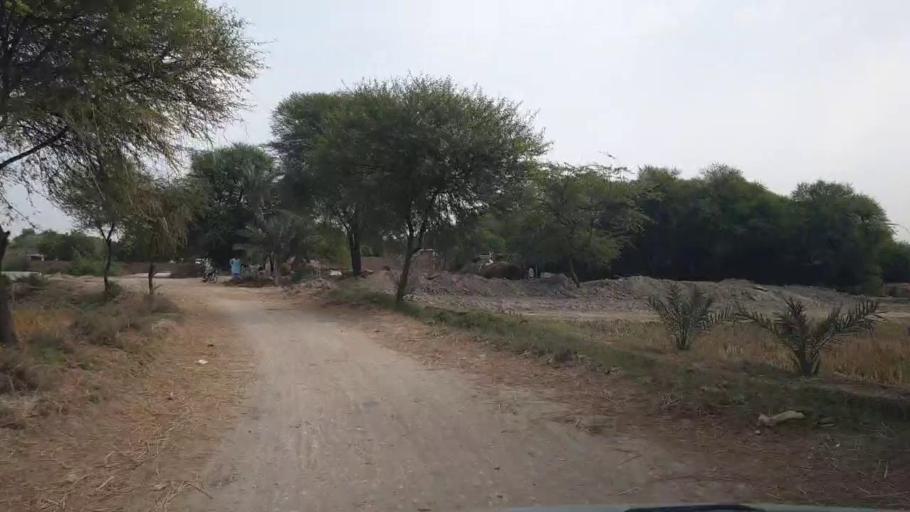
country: PK
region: Sindh
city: Matli
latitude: 24.9572
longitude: 68.7077
